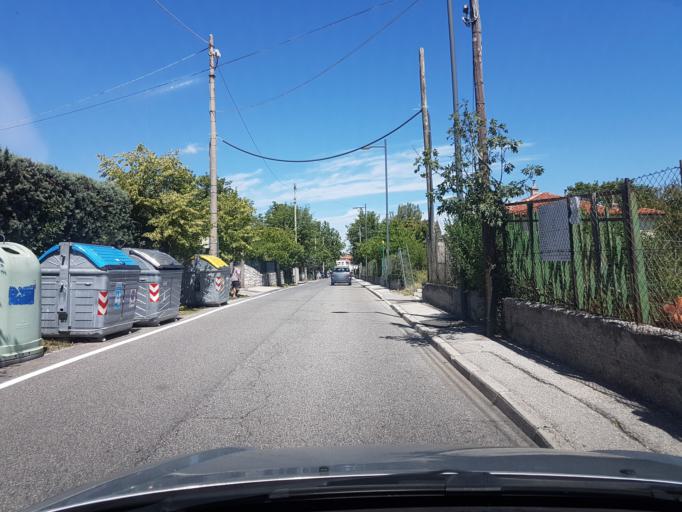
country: IT
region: Friuli Venezia Giulia
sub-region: Provincia di Trieste
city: Prosecco-Contovello
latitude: 45.7059
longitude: 13.7351
